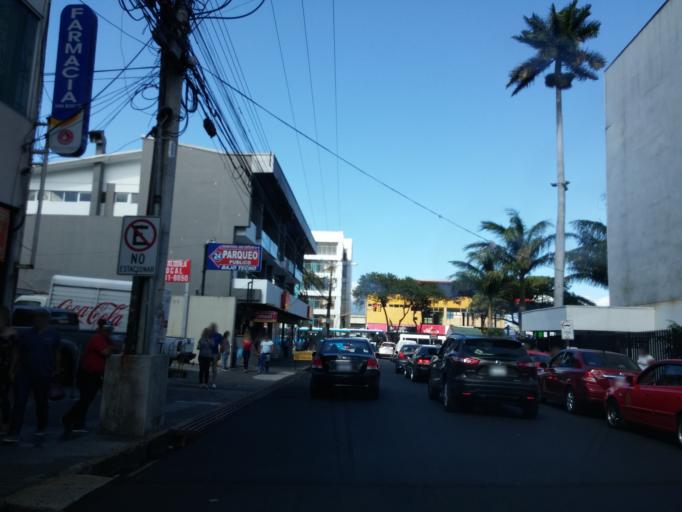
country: CR
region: San Jose
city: San Jose
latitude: 9.9342
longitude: -84.0881
